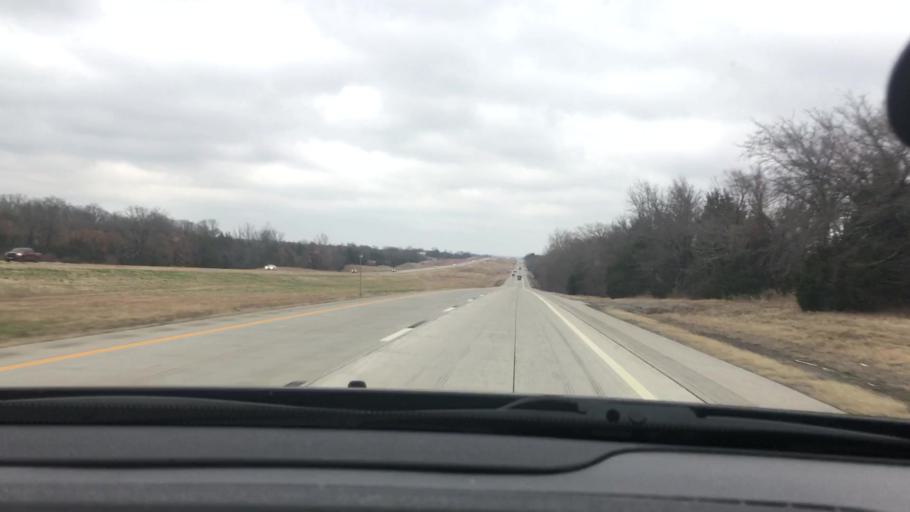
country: US
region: Oklahoma
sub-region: Bryan County
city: Durant
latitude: 34.1786
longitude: -96.2486
